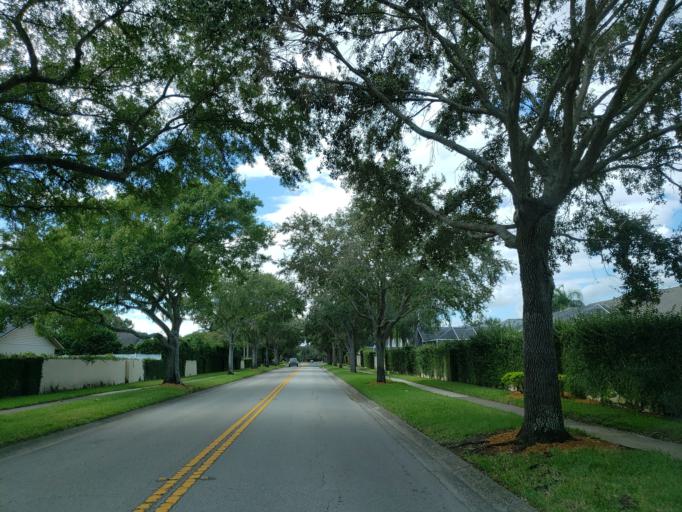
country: US
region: Florida
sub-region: Hillsborough County
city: Bloomingdale
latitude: 27.8740
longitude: -82.2569
